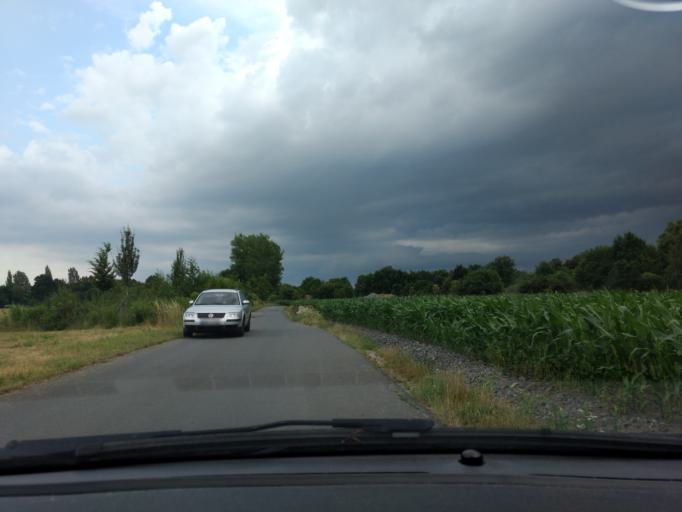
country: DE
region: Saxony
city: Radeburg
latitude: 51.2205
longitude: 13.7374
